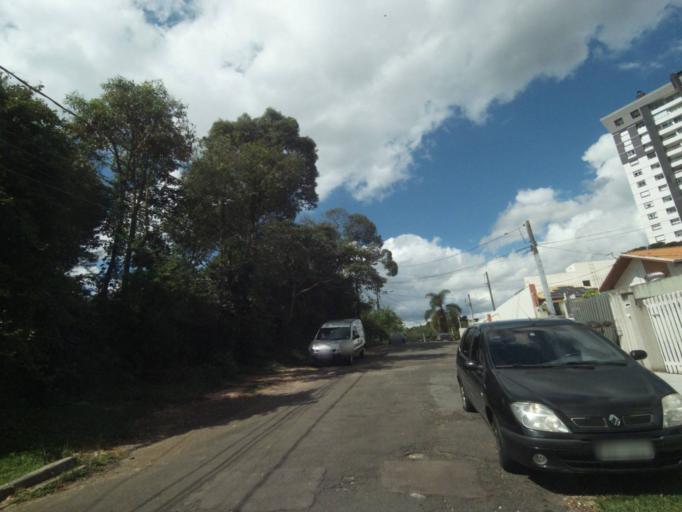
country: BR
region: Parana
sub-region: Curitiba
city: Curitiba
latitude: -25.4366
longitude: -49.3315
